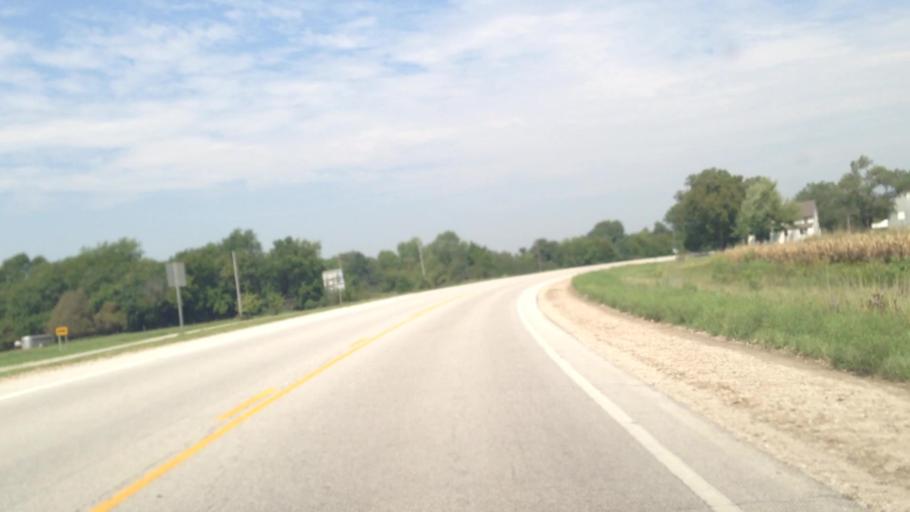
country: US
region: Kansas
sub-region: Labette County
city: Parsons
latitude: 37.3902
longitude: -95.2694
